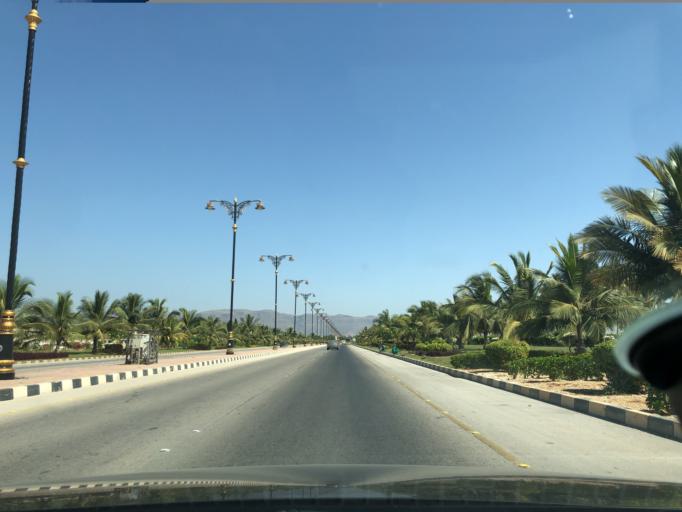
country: OM
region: Zufar
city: Salalah
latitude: 17.0456
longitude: 54.2095
